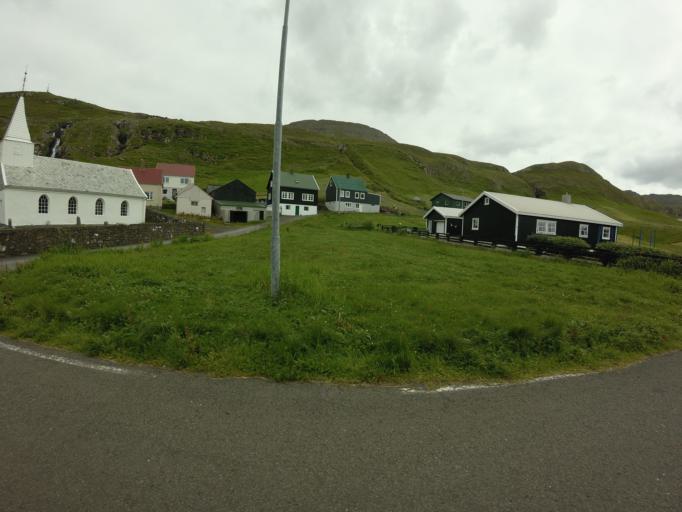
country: FO
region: Suduroy
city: Tvoroyri
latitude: 61.5254
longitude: -6.8799
